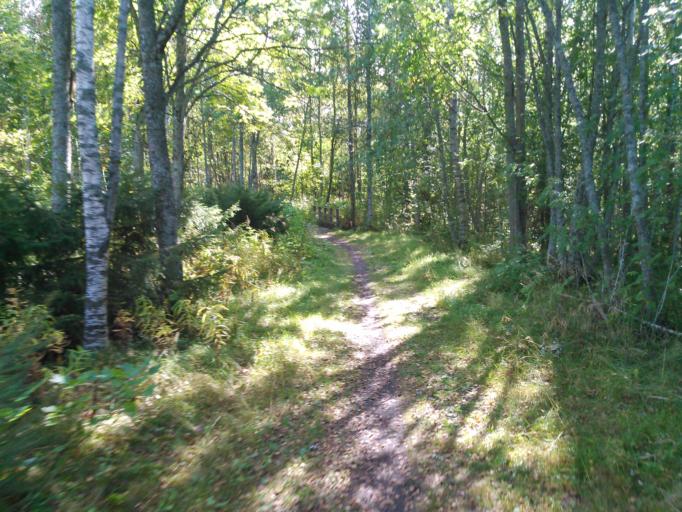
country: SE
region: Vaesterbotten
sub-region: Umea Kommun
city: Umea
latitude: 63.7959
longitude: 20.3200
